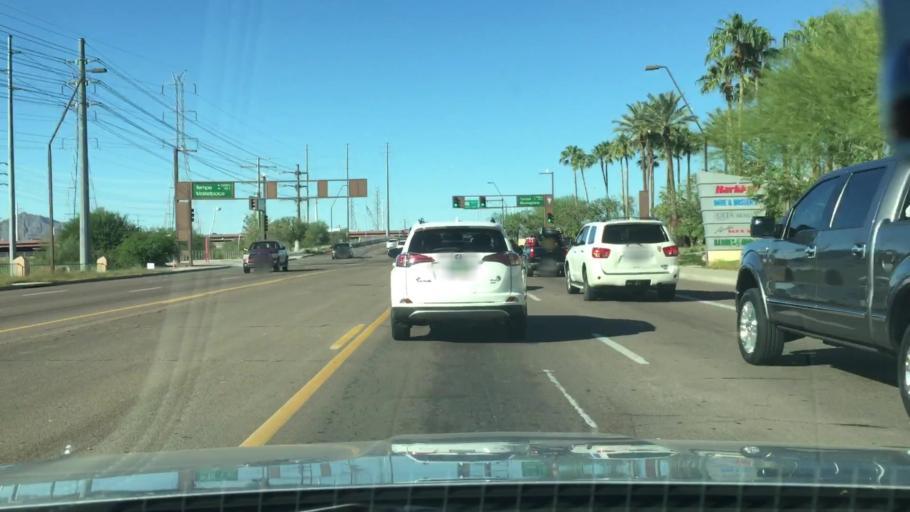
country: US
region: Arizona
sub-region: Maricopa County
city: Tempe
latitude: 33.4312
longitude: -111.9092
